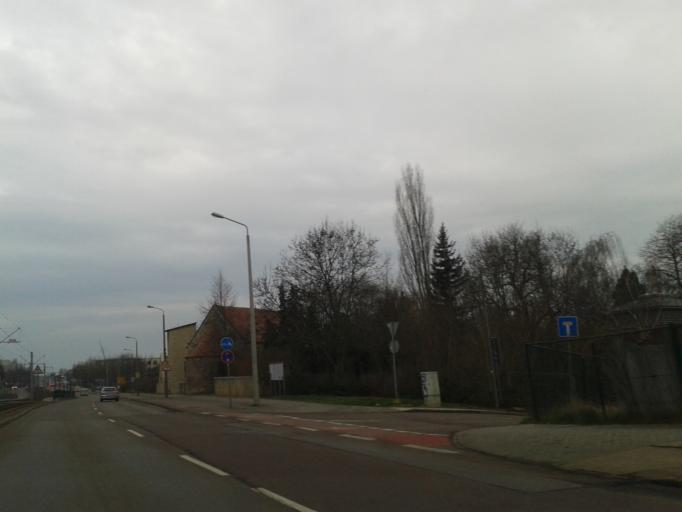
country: DE
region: Saxony-Anhalt
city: Halle Neustadt
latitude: 51.4629
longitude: 11.9513
